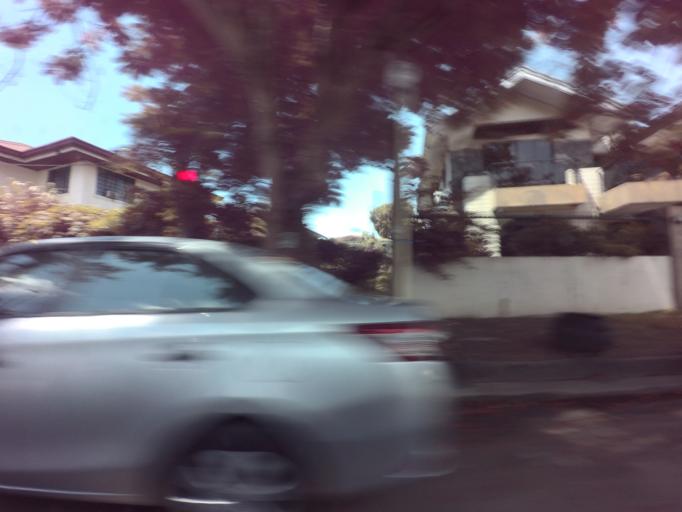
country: PH
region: Calabarzon
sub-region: Province of Rizal
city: Las Pinas
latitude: 14.4281
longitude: 120.9866
